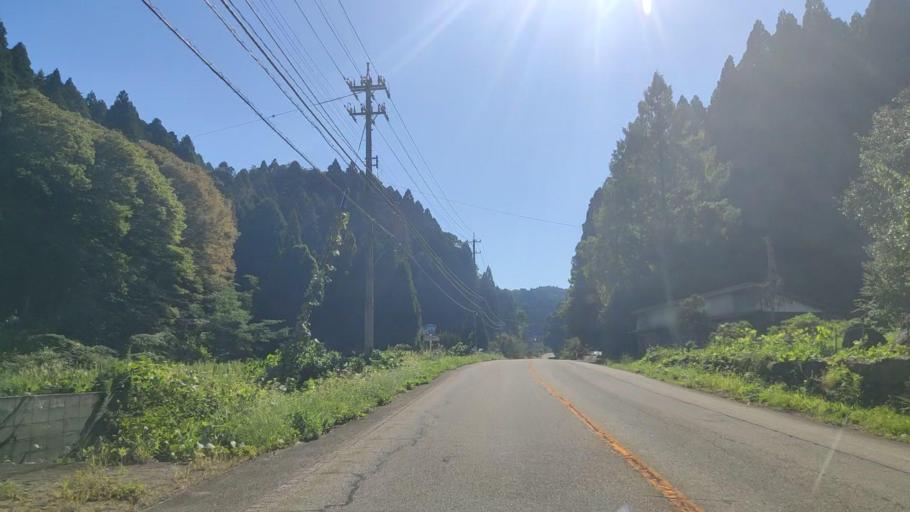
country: JP
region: Ishikawa
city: Nanao
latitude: 37.3248
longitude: 137.1929
